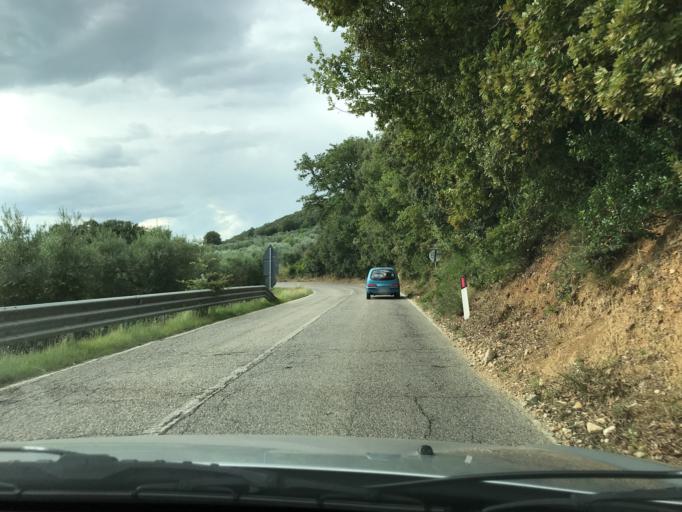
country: IT
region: Umbria
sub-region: Provincia di Terni
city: Guardea
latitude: 42.6384
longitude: 12.2918
